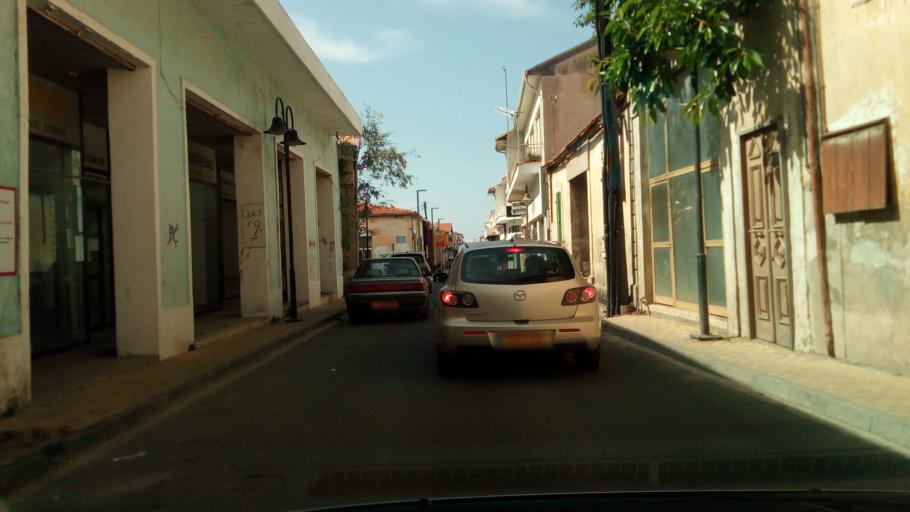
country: CY
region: Pafos
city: Paphos
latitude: 34.7810
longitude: 32.4215
